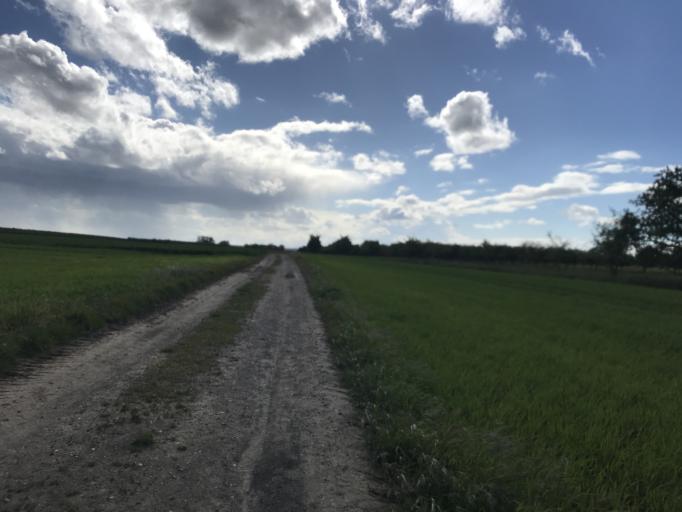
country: DE
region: Rheinland-Pfalz
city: Wackernheim
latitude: 49.9617
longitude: 8.1173
